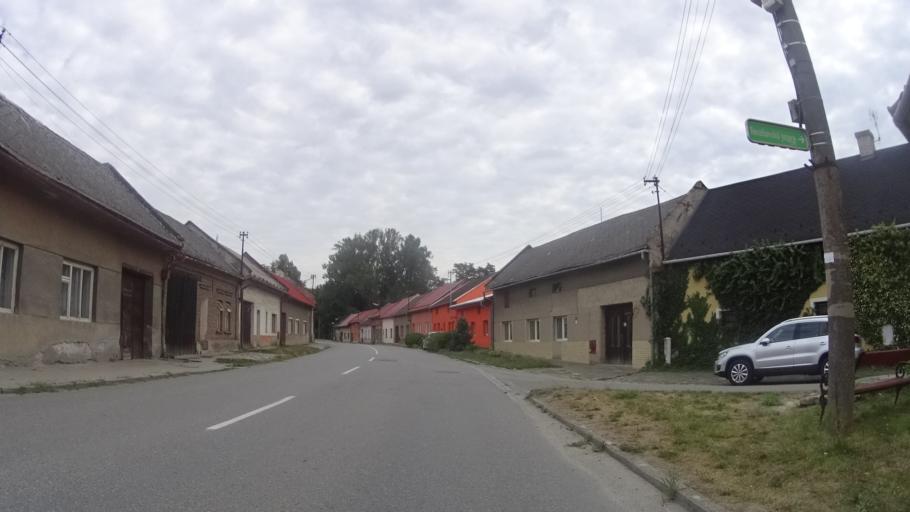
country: CZ
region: Olomoucky
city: Tovacov
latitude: 49.4191
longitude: 17.2880
